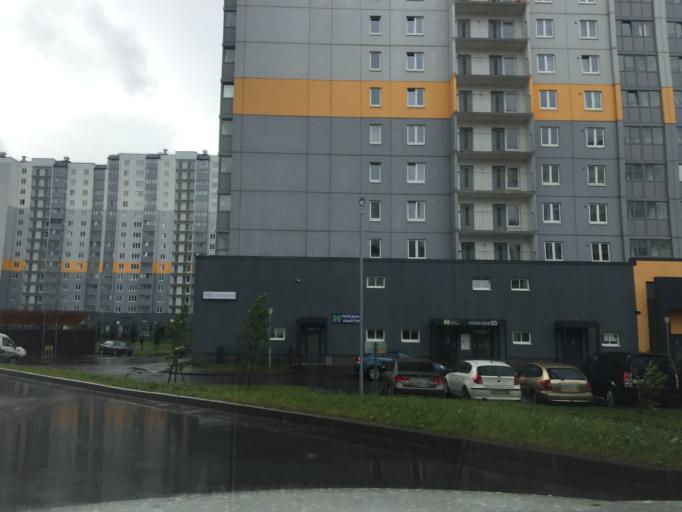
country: RU
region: St.-Petersburg
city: Sosnovaya Polyana
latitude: 59.7905
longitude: 30.1662
